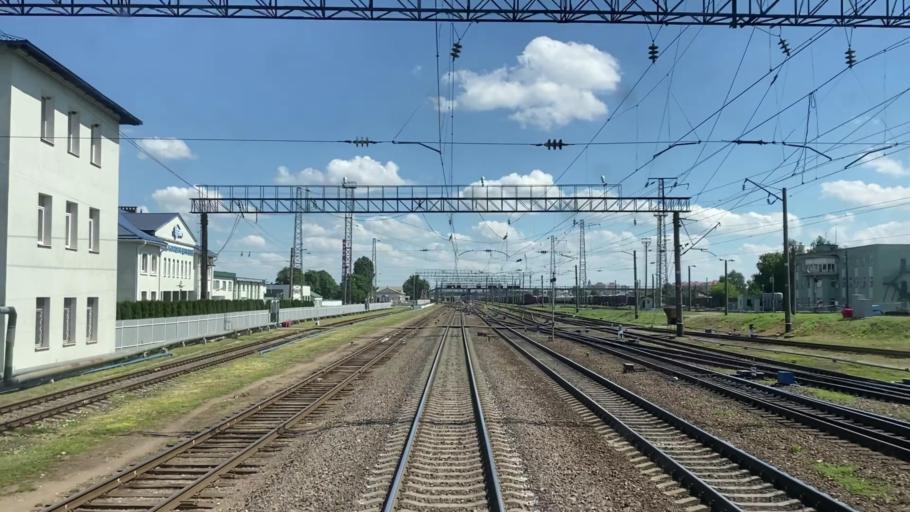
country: BY
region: Brest
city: Baranovichi
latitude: 53.1304
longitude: 25.9886
